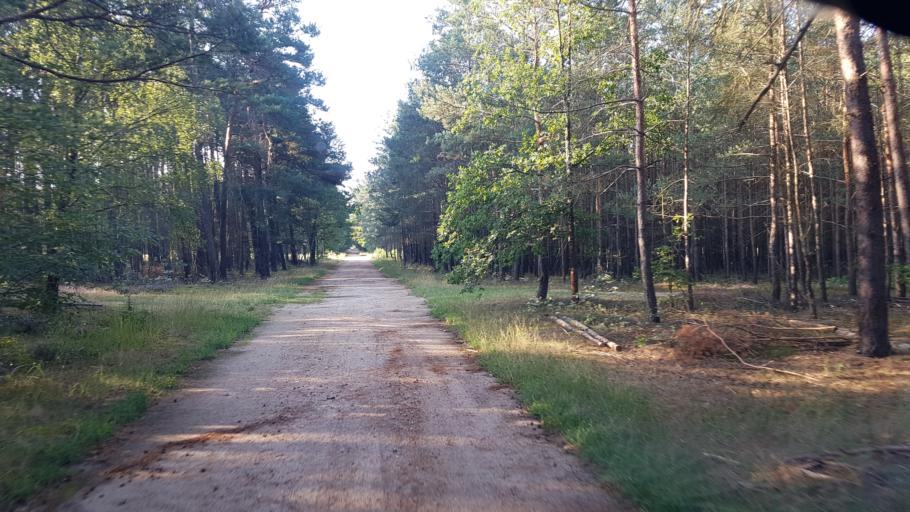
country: DE
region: Brandenburg
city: Sonnewalde
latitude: 51.6609
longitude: 13.6454
